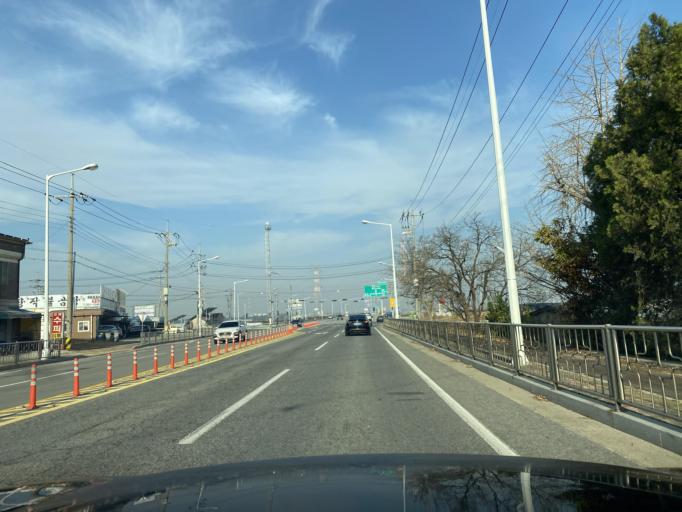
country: KR
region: Chungcheongnam-do
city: Yesan
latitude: 36.7380
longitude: 126.8600
